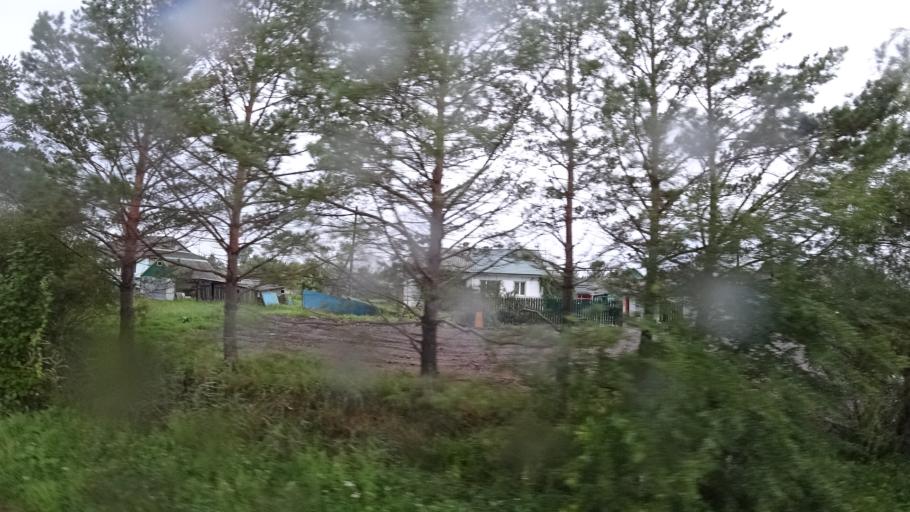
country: RU
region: Primorskiy
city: Chernigovka
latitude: 44.4092
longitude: 132.5327
